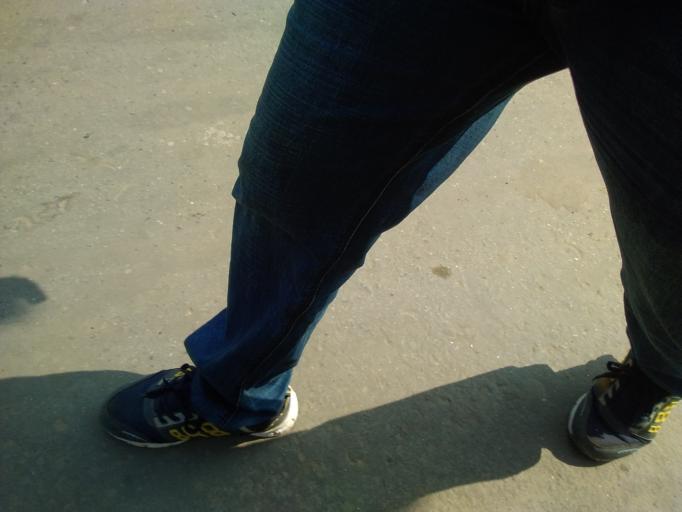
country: BD
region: Khulna
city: Khulna
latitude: 22.8060
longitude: 89.5773
